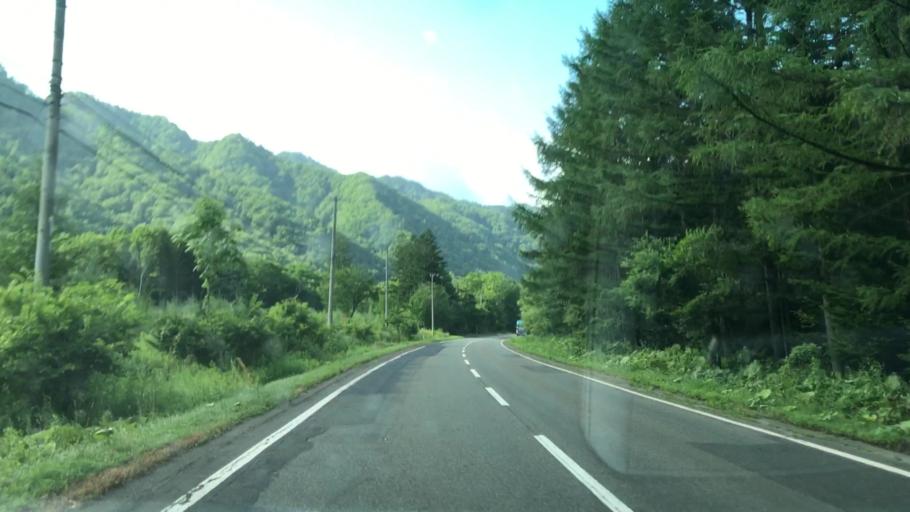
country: JP
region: Hokkaido
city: Shizunai-furukawacho
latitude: 42.8238
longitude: 142.4172
